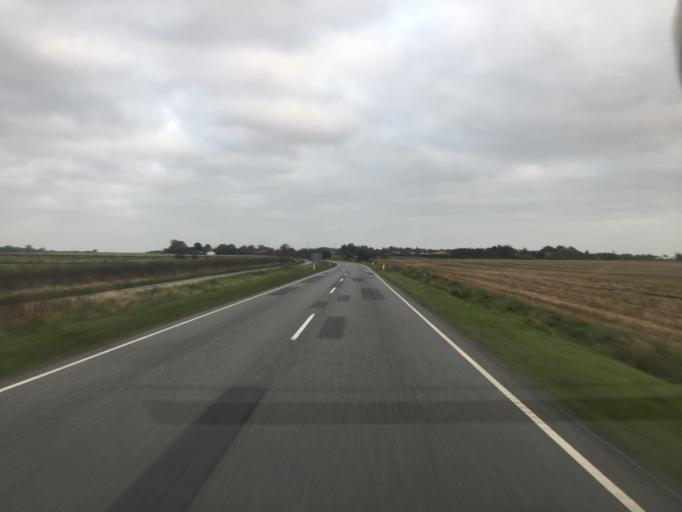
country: DE
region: Schleswig-Holstein
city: Aventoft
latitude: 54.9519
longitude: 8.7826
